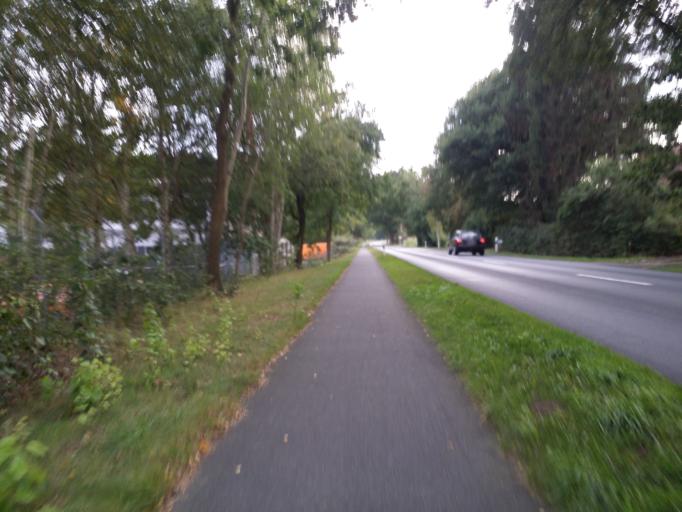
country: DE
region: Lower Saxony
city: Bremervorde
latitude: 53.4668
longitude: 9.1260
